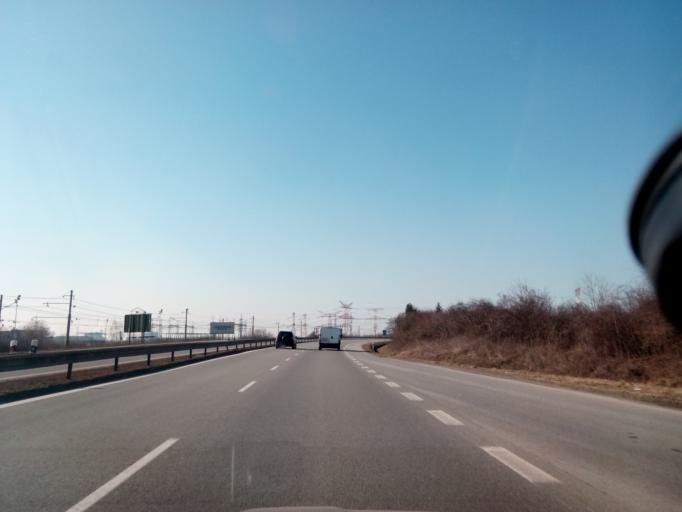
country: SK
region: Kosicky
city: Kosice
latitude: 48.6329
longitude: 21.1939
